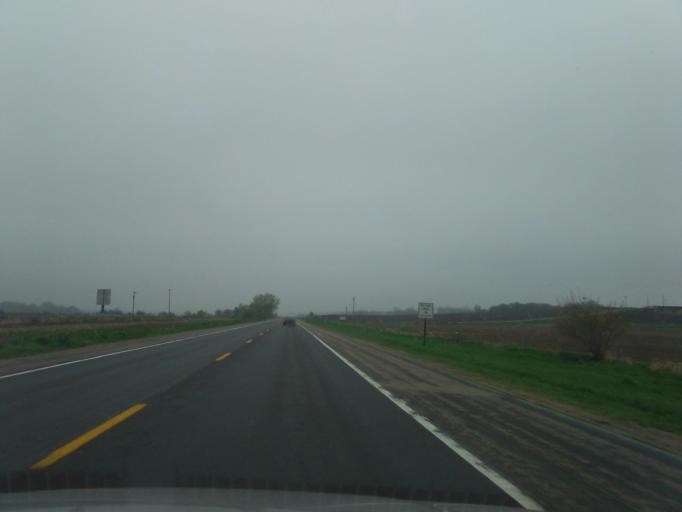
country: US
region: Nebraska
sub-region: Cuming County
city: Wisner
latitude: 41.9450
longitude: -96.8425
